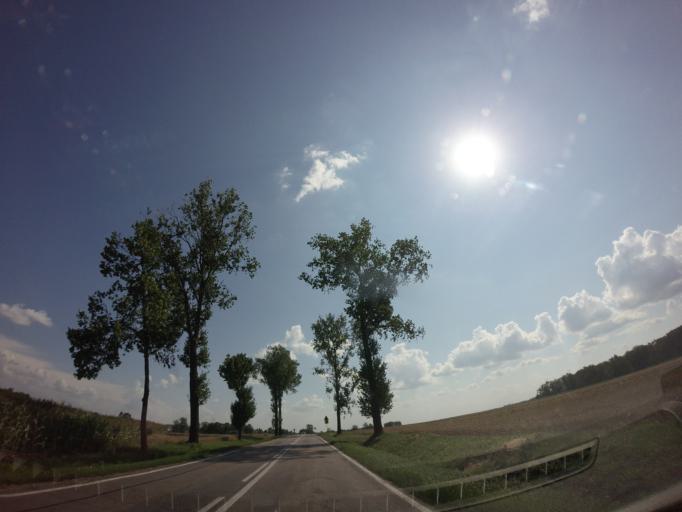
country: PL
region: Podlasie
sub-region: Powiat zambrowski
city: Zambrow
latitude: 52.8924
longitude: 22.2511
